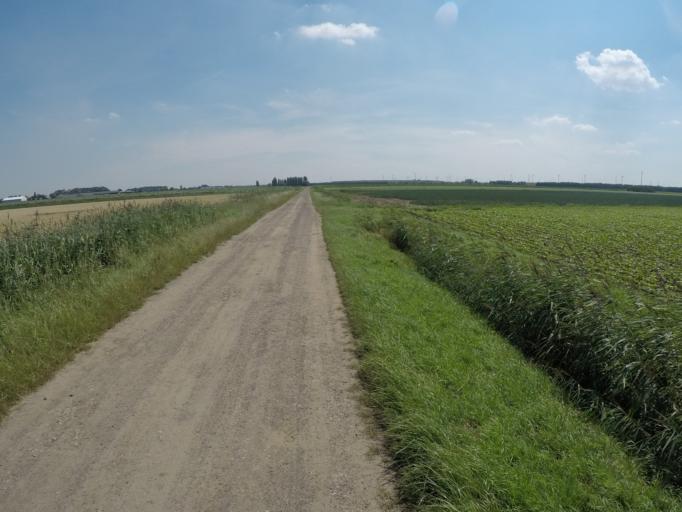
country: BE
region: Flanders
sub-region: Provincie Antwerpen
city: Stabroek
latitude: 51.3167
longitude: 4.3741
